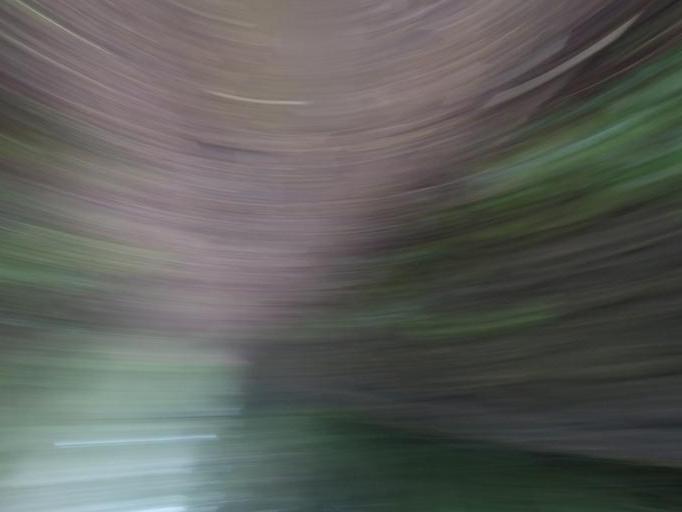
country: PT
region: Madeira
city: Ponta do Sol
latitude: 32.7105
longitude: -17.0931
